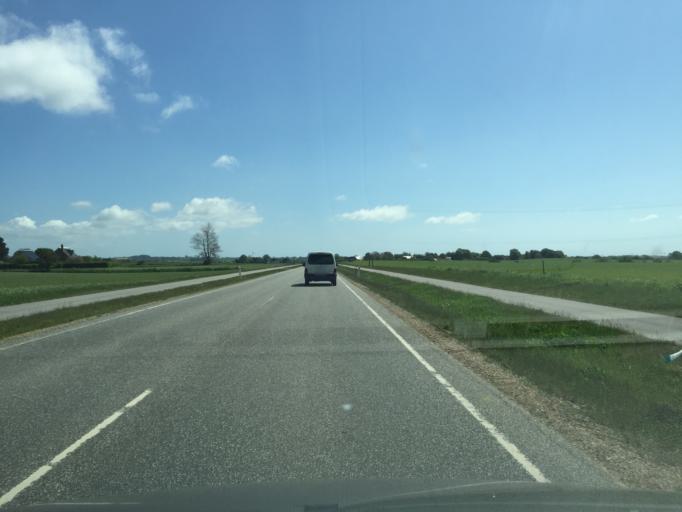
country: DK
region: Zealand
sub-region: Vordingborg Kommune
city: Stege
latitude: 54.9799
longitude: 12.1825
